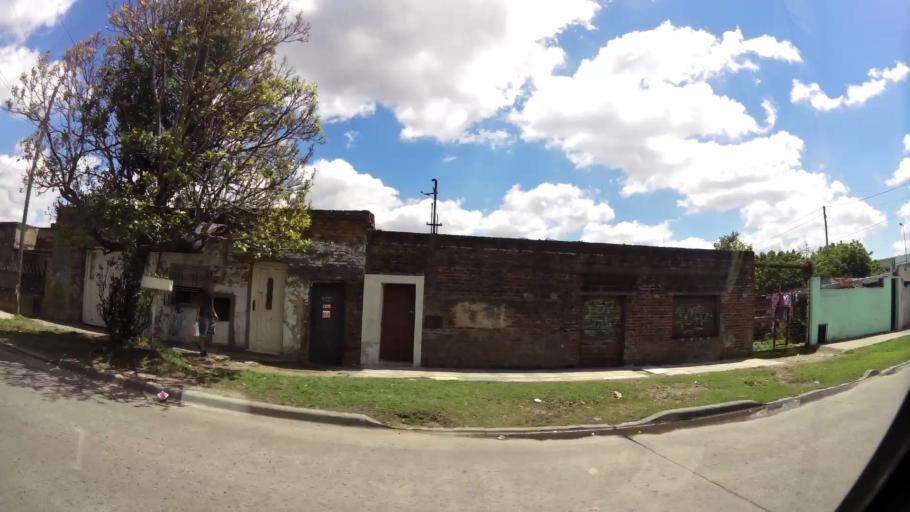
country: AR
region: Buenos Aires
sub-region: Partido de Lanus
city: Lanus
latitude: -34.7004
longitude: -58.4348
